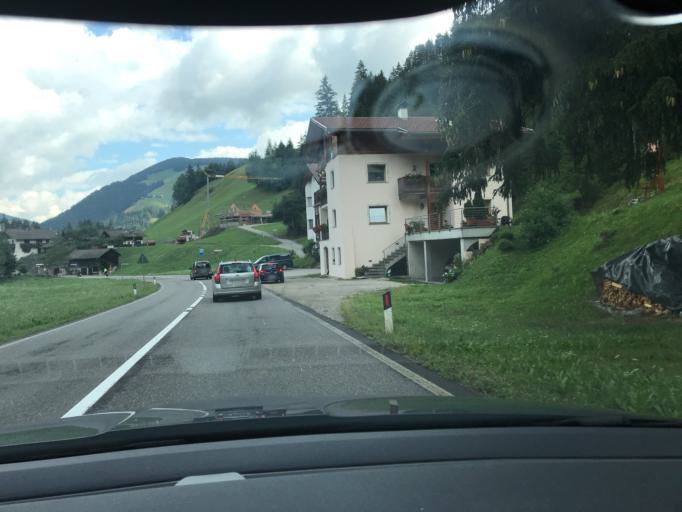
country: IT
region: Trentino-Alto Adige
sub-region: Bolzano
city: San Martino in Badia
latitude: 46.6729
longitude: 11.9026
